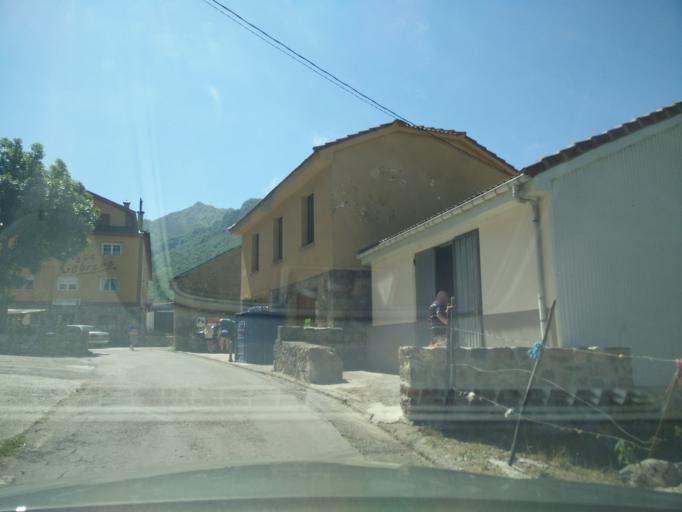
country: ES
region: Asturias
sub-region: Province of Asturias
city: Pola de Somiedo
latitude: 43.0722
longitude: -6.1994
